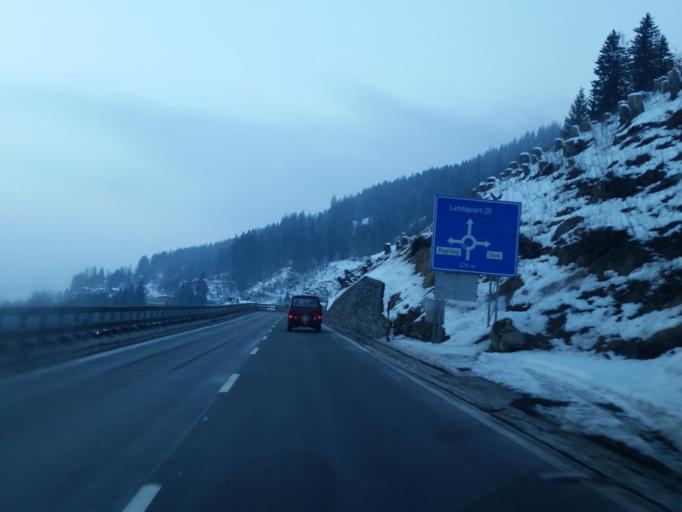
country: CH
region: Grisons
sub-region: Praettigau/Davos District
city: Klosters Serneus
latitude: 46.8986
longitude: 9.8366
